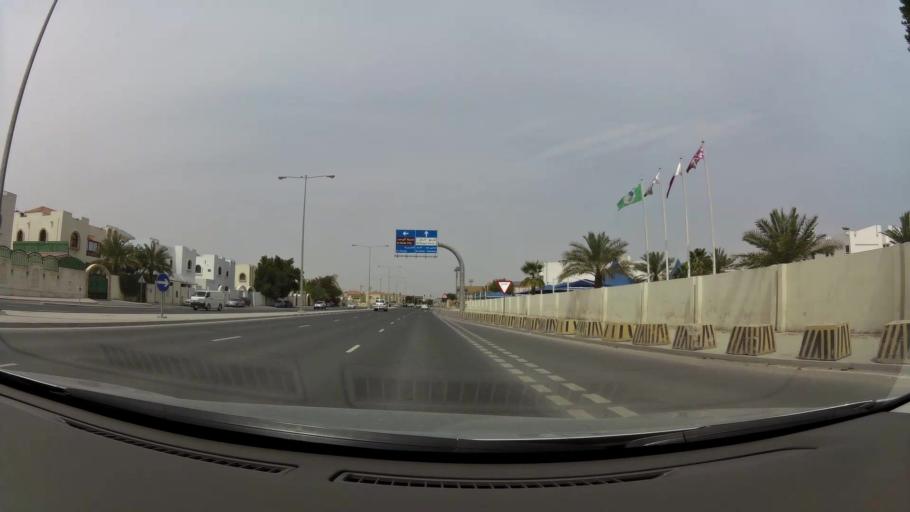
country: QA
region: Baladiyat ad Dawhah
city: Doha
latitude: 25.2597
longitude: 51.4826
